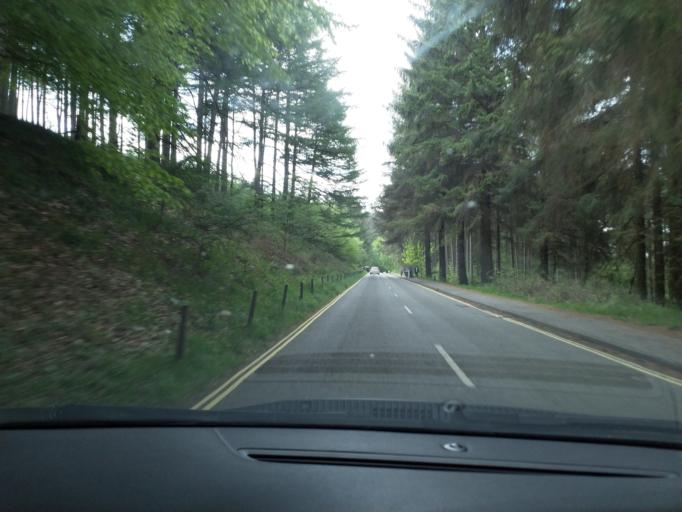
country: GB
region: England
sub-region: Derbyshire
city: Hope Valley
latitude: 53.3950
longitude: -1.7376
